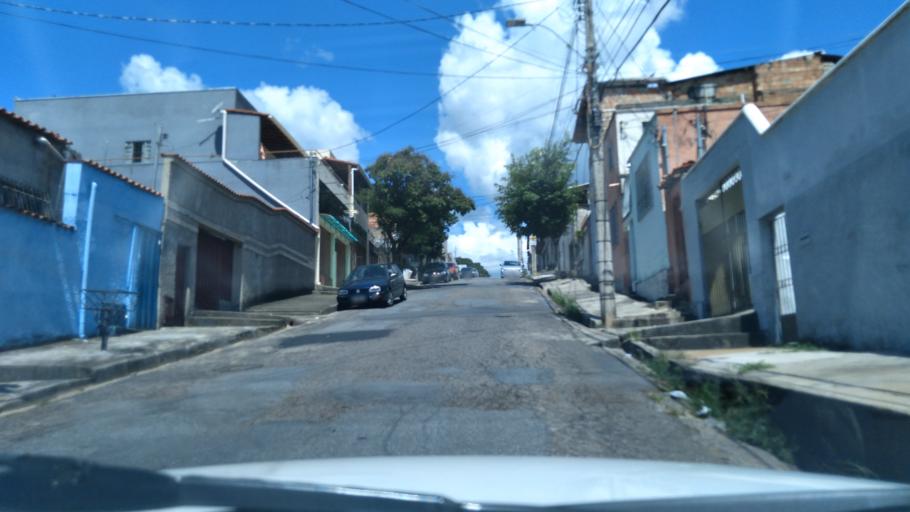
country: BR
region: Minas Gerais
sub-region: Belo Horizonte
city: Belo Horizonte
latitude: -19.8657
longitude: -43.9176
